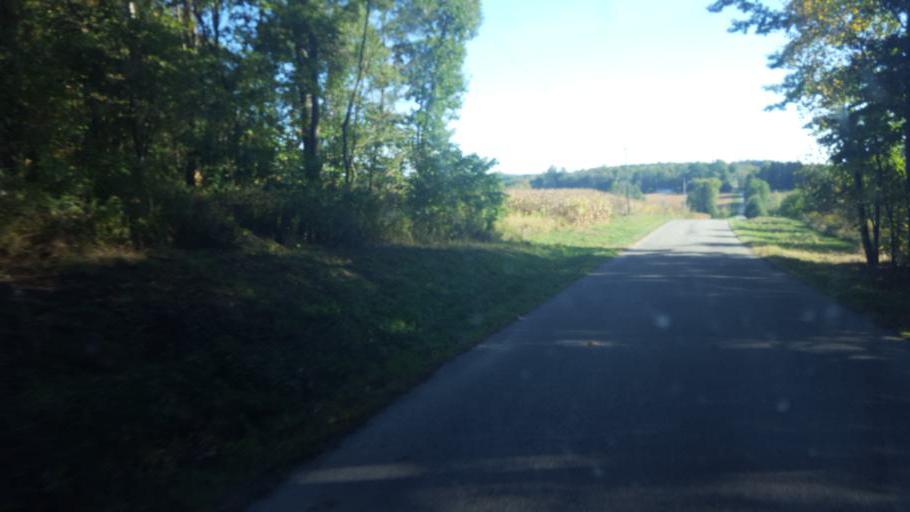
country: US
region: Ohio
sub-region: Richland County
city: Lexington
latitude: 40.6436
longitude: -82.5783
